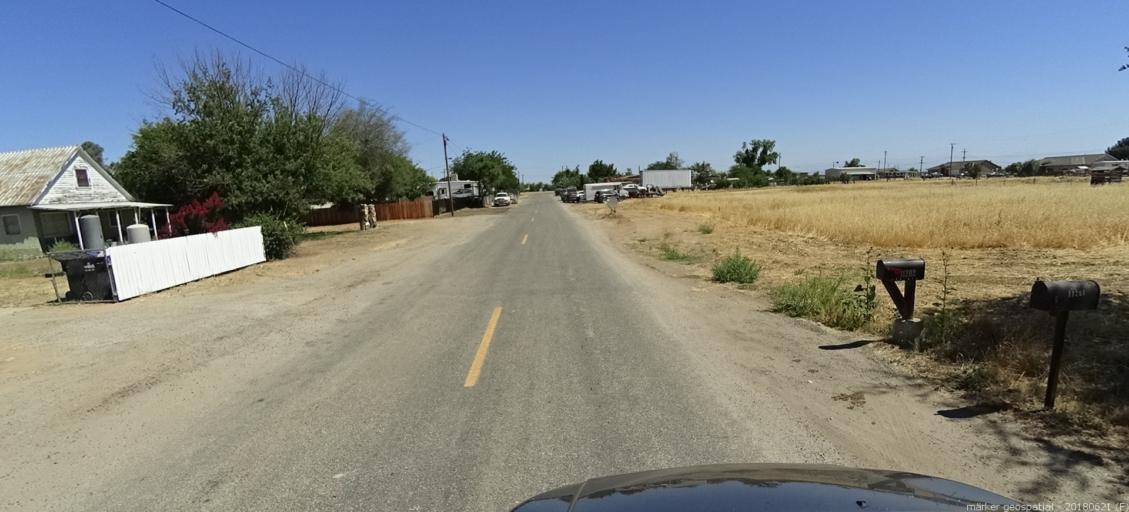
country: US
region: California
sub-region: Madera County
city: Parksdale
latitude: 36.9112
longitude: -119.9602
